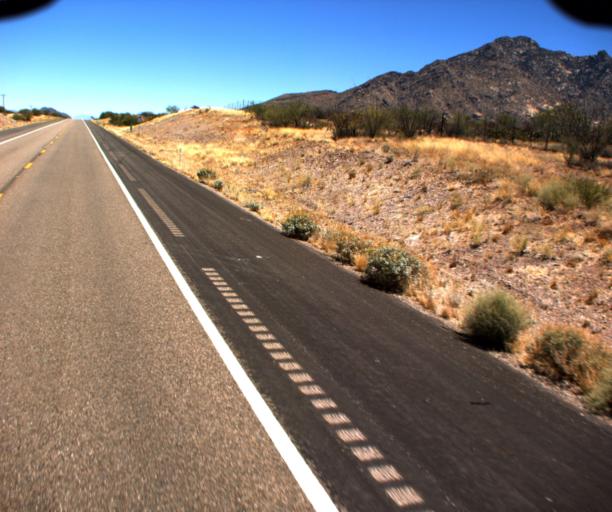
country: US
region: Arizona
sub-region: Pima County
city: Three Points
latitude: 32.0254
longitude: -111.5847
